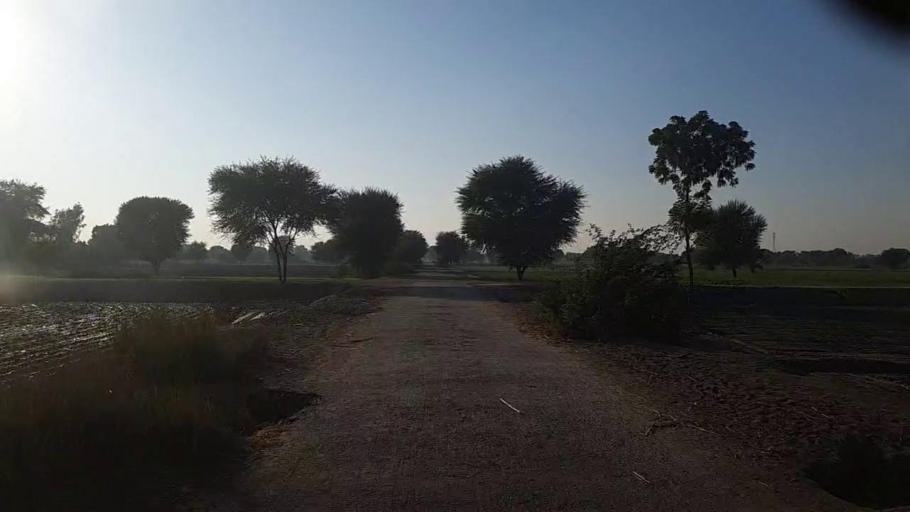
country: PK
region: Sindh
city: Pad Idan
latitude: 26.7342
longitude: 68.3376
